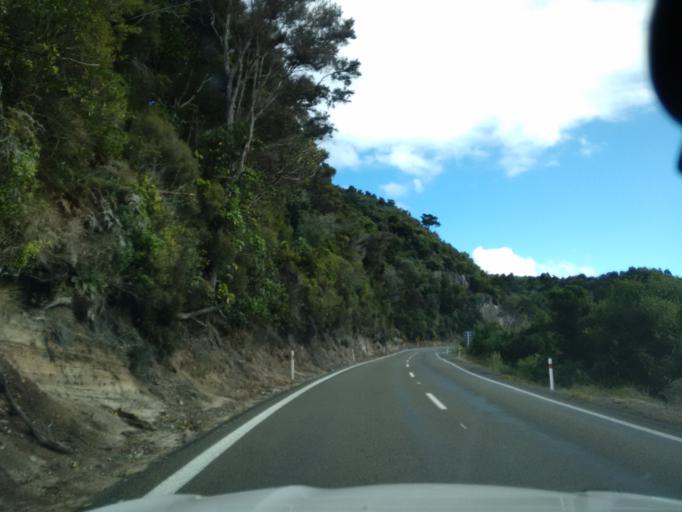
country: NZ
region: Waikato
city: Turangi
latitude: -38.8821
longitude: 175.9703
